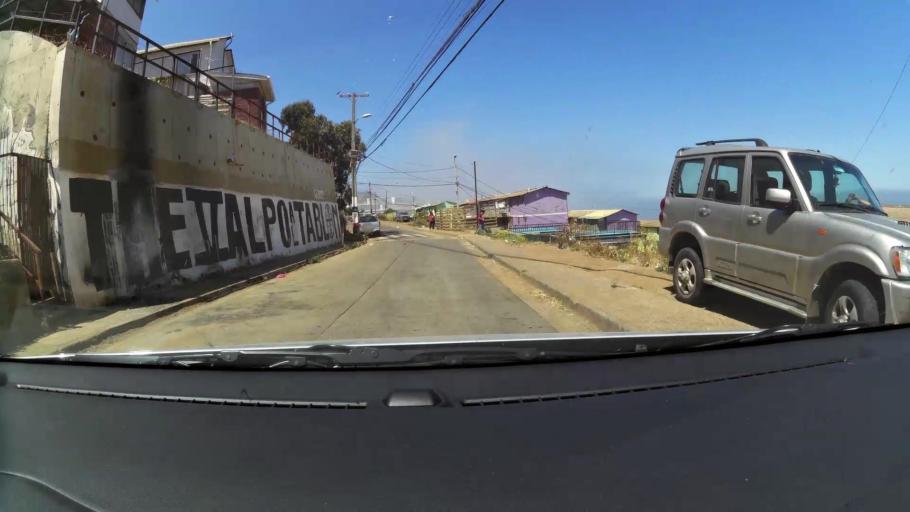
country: CL
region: Valparaiso
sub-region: Provincia de Valparaiso
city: Valparaiso
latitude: -33.0348
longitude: -71.6538
